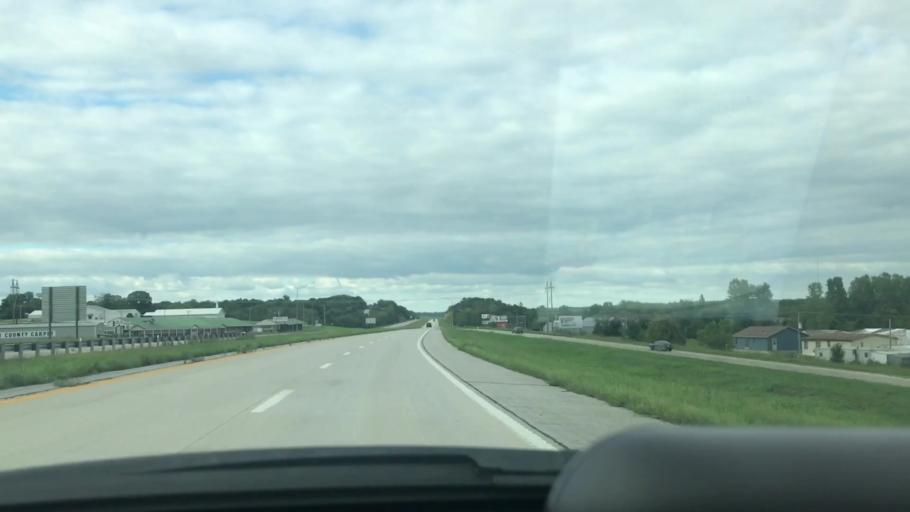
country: US
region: Missouri
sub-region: Benton County
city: Warsaw
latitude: 38.2657
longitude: -93.3682
